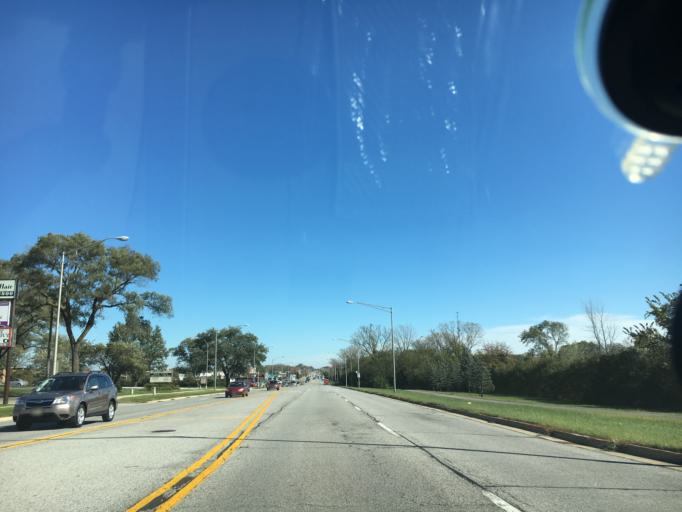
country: US
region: Illinois
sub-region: Cook County
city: Oak Forest
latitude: 41.6027
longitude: -87.7660
